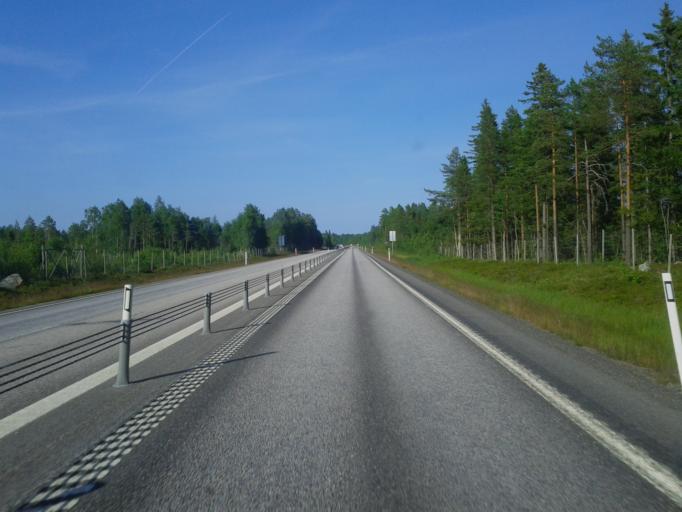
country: SE
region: Vaesterbotten
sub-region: Umea Kommun
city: Saevar
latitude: 63.9618
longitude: 20.6894
